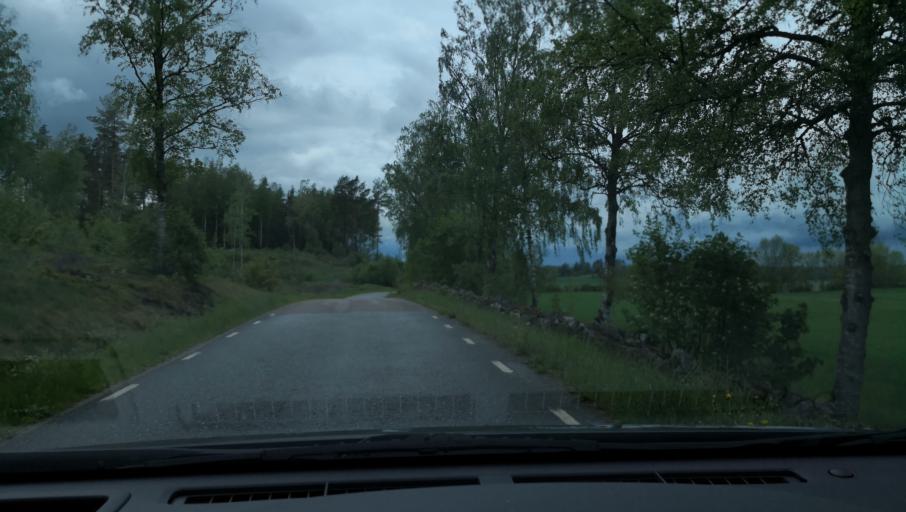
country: SE
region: Uppsala
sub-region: Enkopings Kommun
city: Orsundsbro
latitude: 59.7244
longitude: 17.3805
